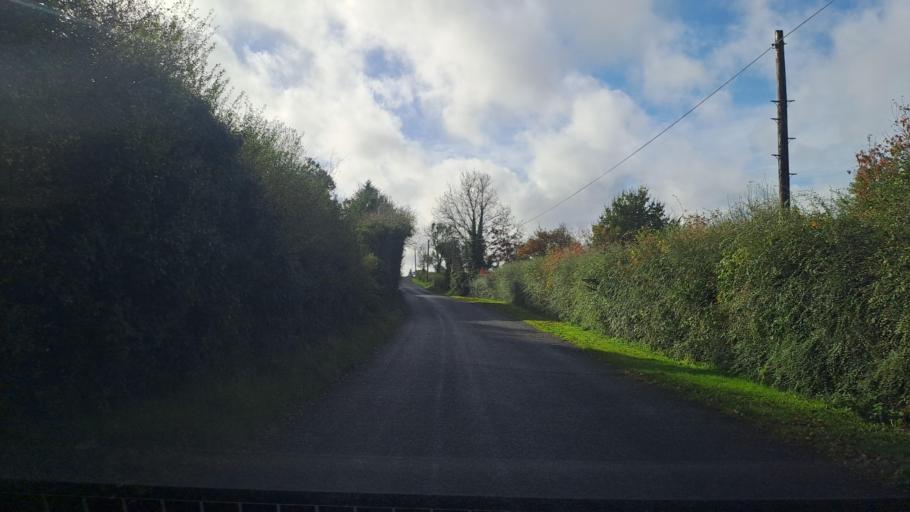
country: IE
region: Ulster
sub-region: An Cabhan
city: Cootehill
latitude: 54.0333
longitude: -7.0162
